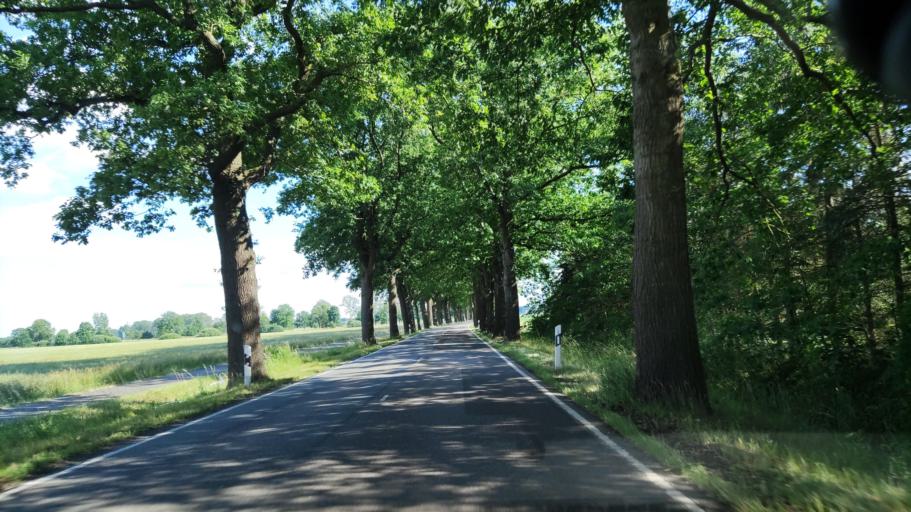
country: DE
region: Mecklenburg-Vorpommern
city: Domitz
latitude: 53.1618
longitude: 11.2415
